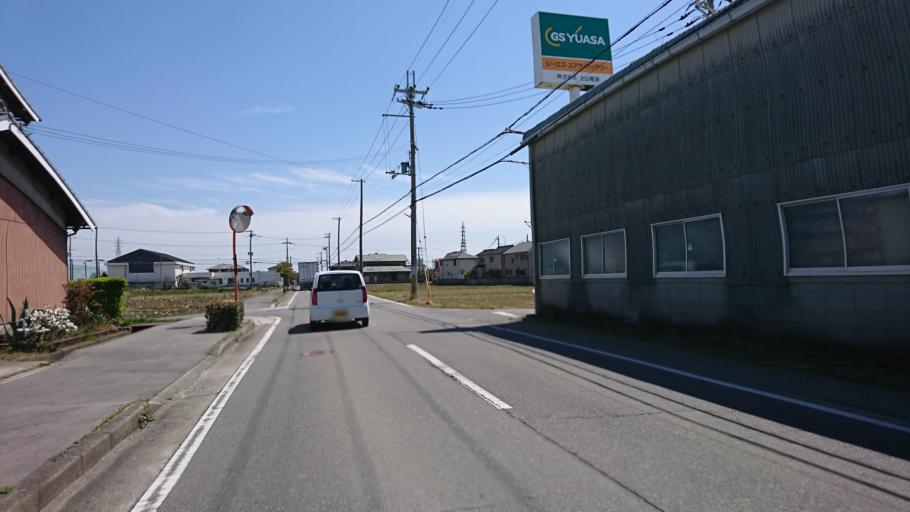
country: JP
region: Hyogo
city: Kakogawacho-honmachi
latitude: 34.7353
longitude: 134.8978
